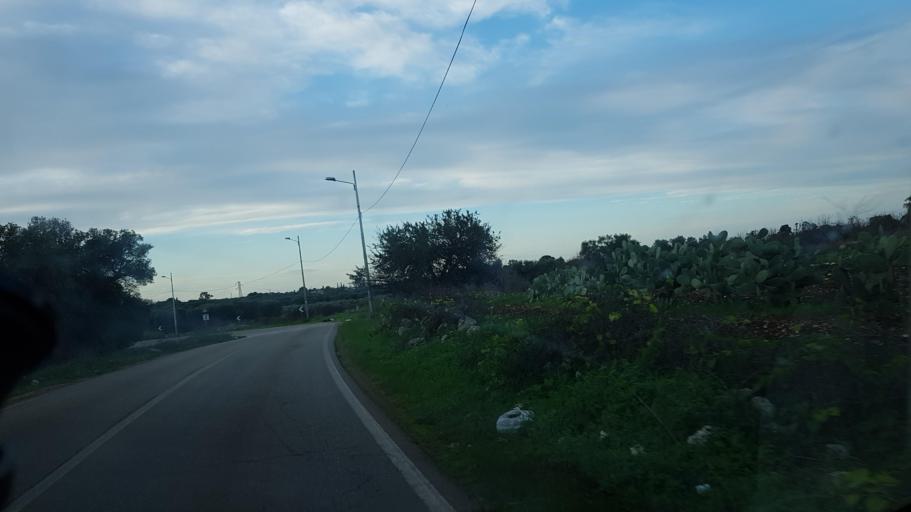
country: IT
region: Apulia
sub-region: Provincia di Brindisi
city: San Vito dei Normanni
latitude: 40.6498
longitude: 17.6935
